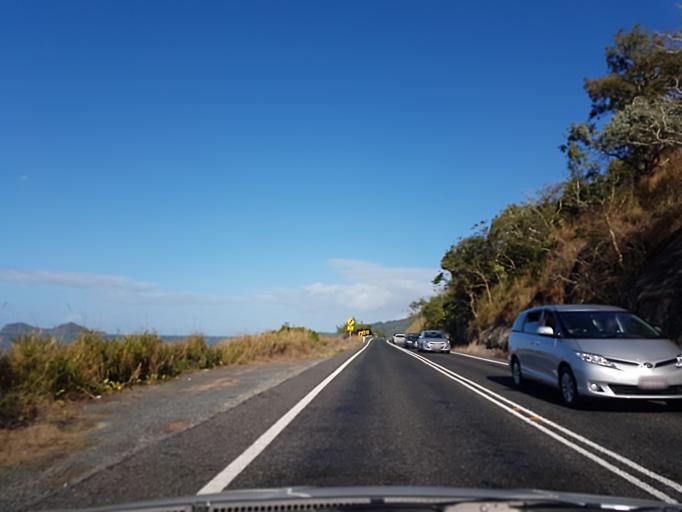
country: AU
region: Queensland
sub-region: Cairns
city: Palm Cove
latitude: -16.7158
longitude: 145.6373
